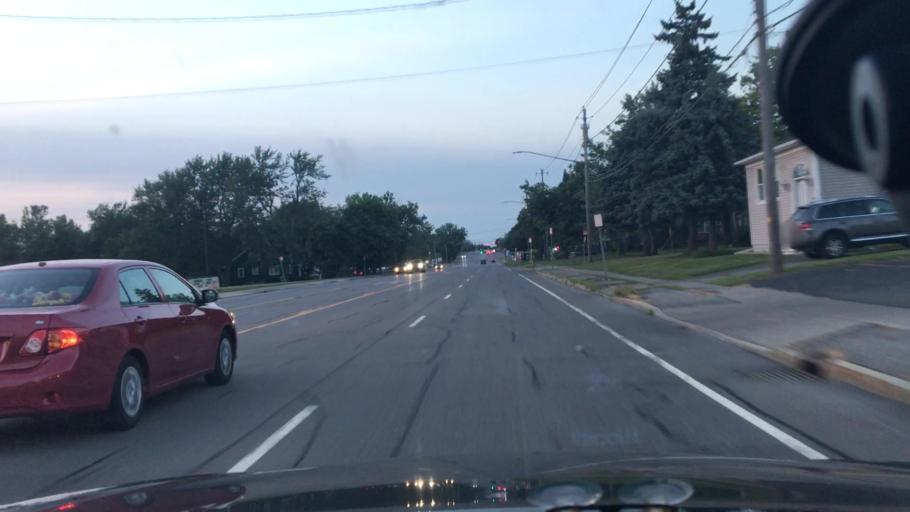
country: US
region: New York
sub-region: Erie County
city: Cheektowaga
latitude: 42.8606
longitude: -78.7544
